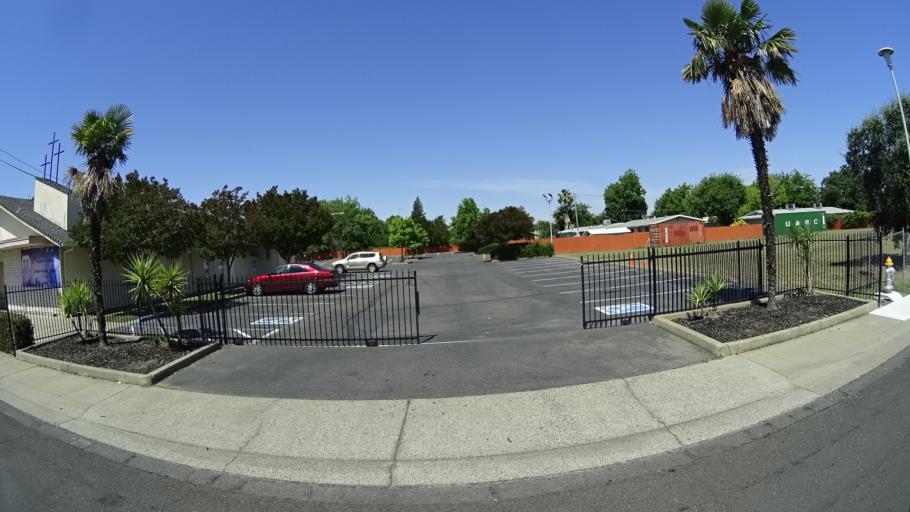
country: US
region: California
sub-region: Sacramento County
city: Florin
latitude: 38.5349
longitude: -121.4143
